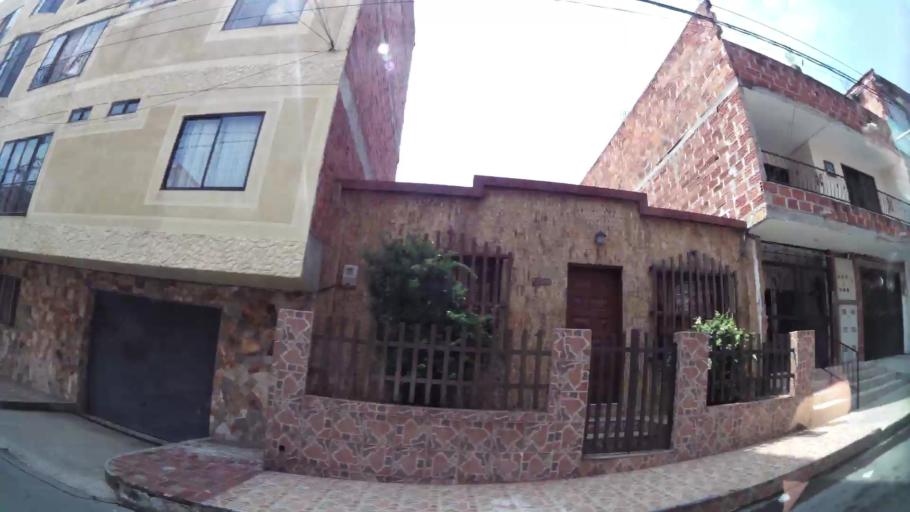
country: CO
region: Antioquia
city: Bello
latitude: 6.3216
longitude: -75.5609
